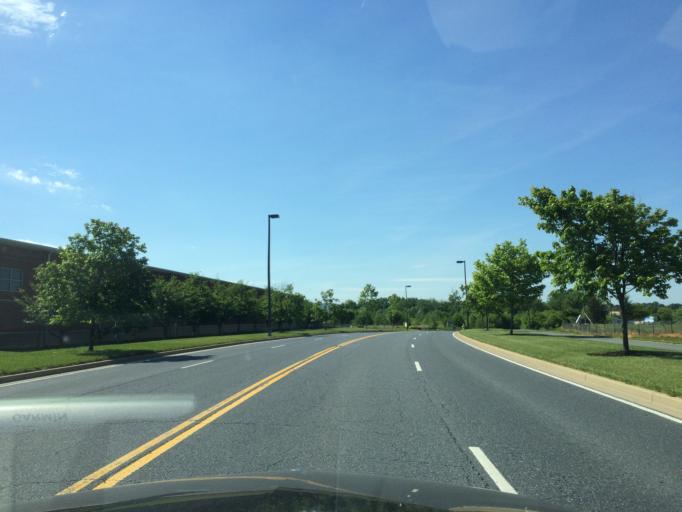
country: US
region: Maryland
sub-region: Frederick County
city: Frederick
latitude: 39.4397
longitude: -77.3811
